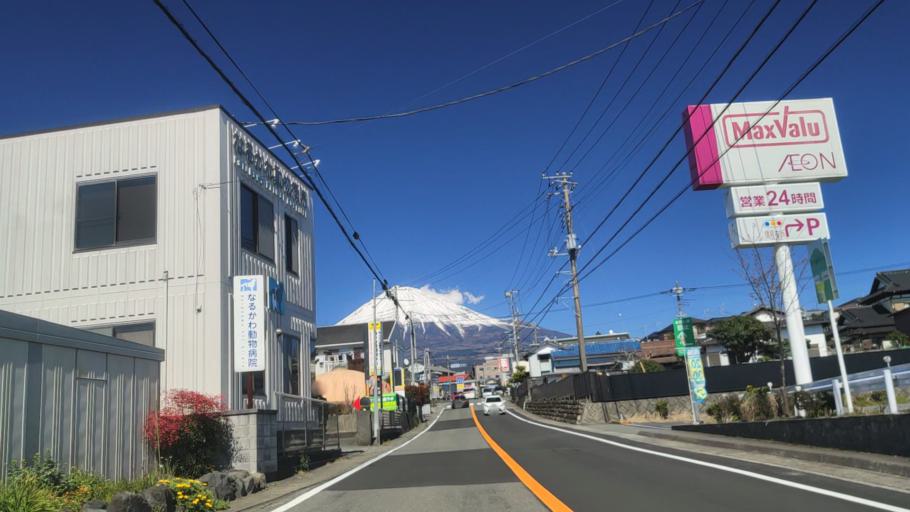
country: JP
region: Shizuoka
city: Fujinomiya
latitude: 35.2151
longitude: 138.6376
